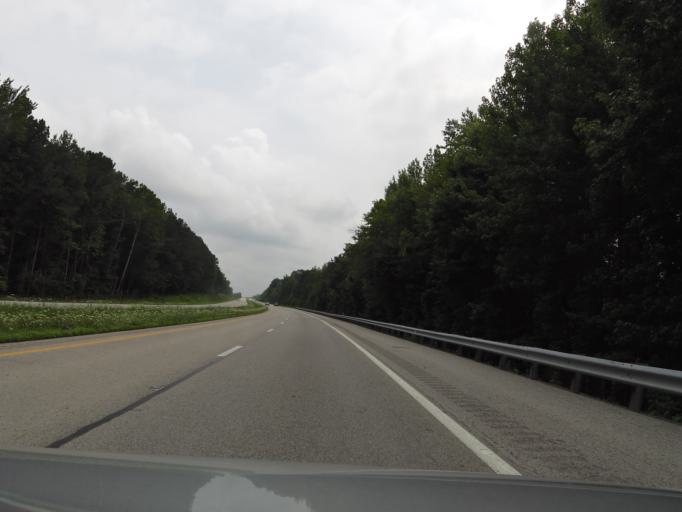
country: US
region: Kentucky
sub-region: Ohio County
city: Beaver Dam
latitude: 37.3523
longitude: -86.8923
